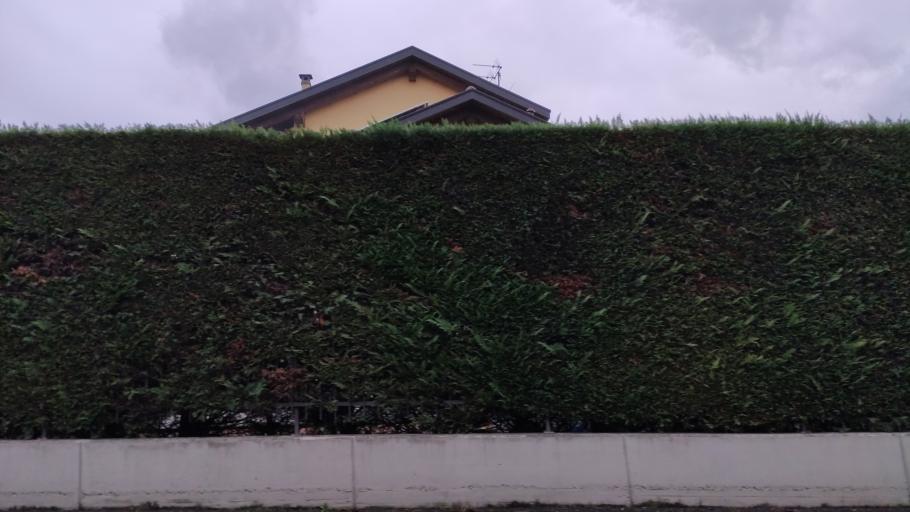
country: IT
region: Piedmont
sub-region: Provincia di Torino
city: Settimo Torinese
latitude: 45.1466
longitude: 7.7695
